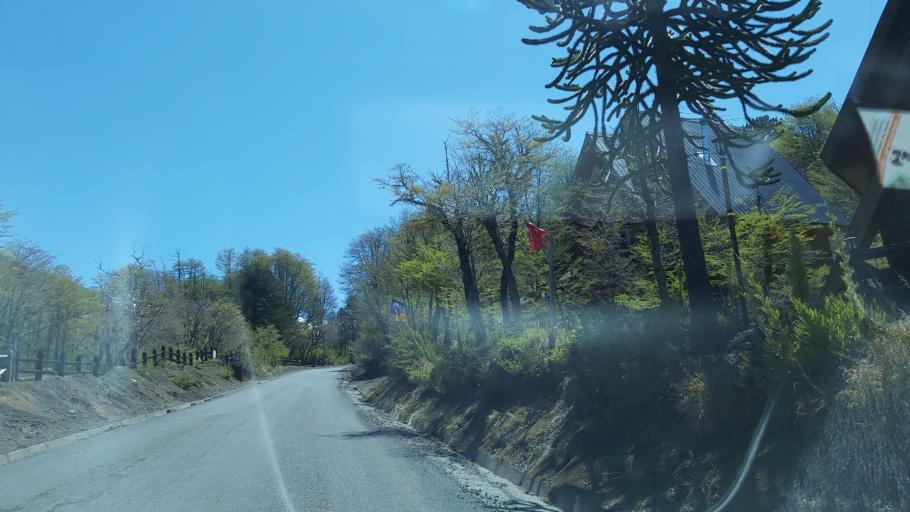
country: CL
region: Araucania
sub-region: Provincia de Cautin
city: Vilcun
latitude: -38.4362
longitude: -71.5327
